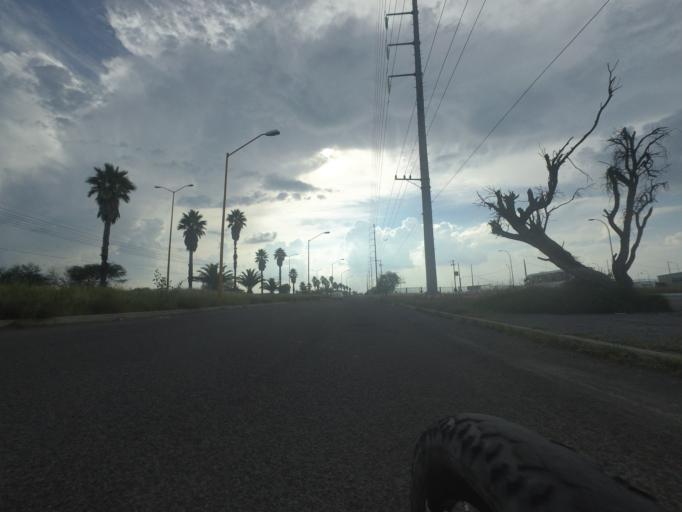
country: MX
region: Aguascalientes
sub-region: Aguascalientes
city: Penuelas (El Cienegal)
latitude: 21.7254
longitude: -102.2986
